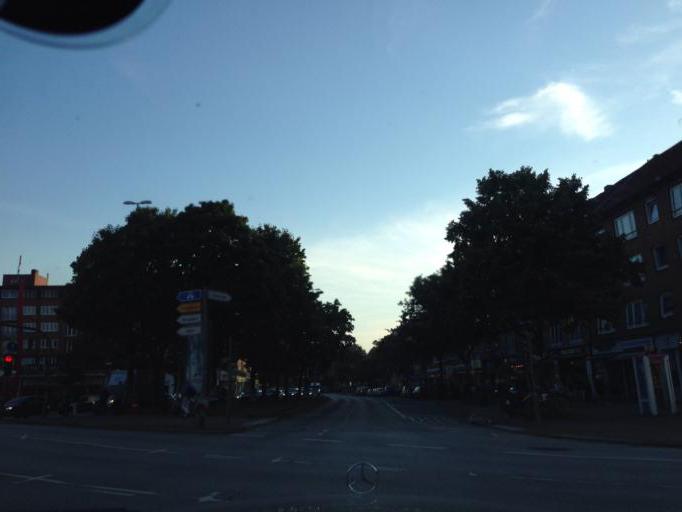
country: DE
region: Hamburg
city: Hamburg
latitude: 53.5703
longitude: 10.0271
